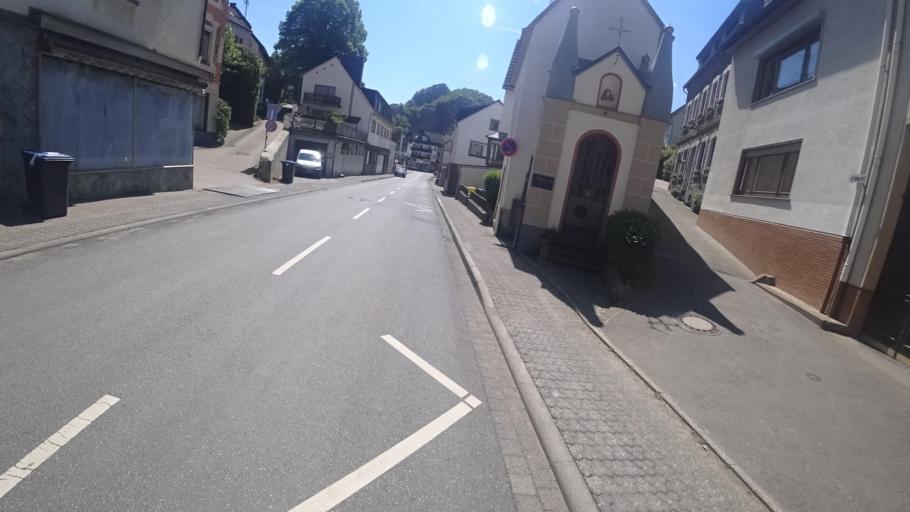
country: DE
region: Rheinland-Pfalz
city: Altenahr
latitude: 50.5181
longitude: 6.9929
